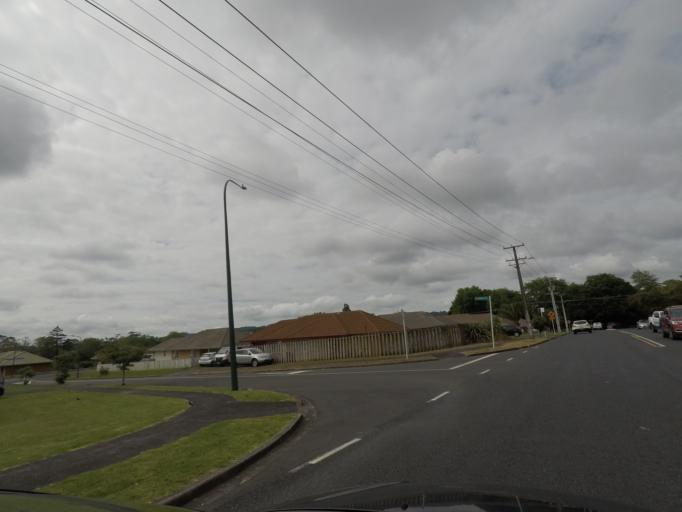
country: NZ
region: Auckland
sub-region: Auckland
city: Waitakere
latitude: -36.9025
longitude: 174.6215
